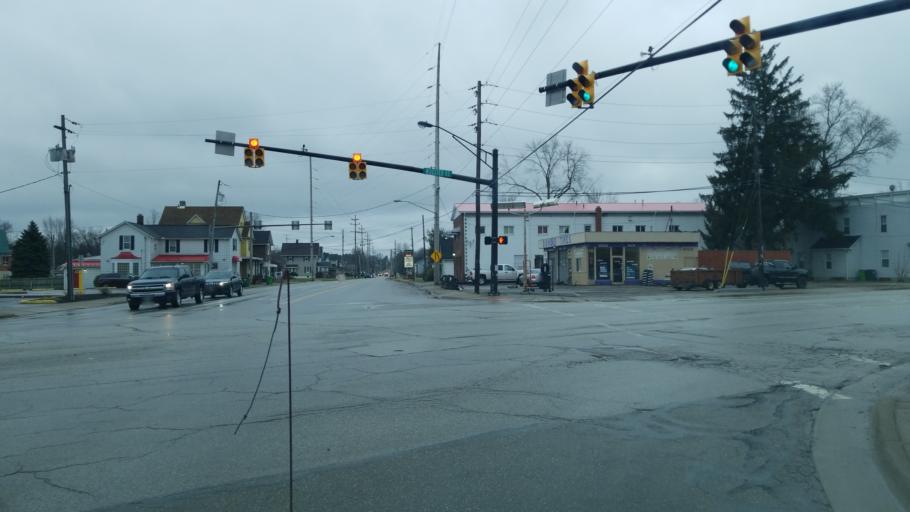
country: US
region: Ohio
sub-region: Summit County
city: Norton
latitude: 41.0058
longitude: -81.6387
